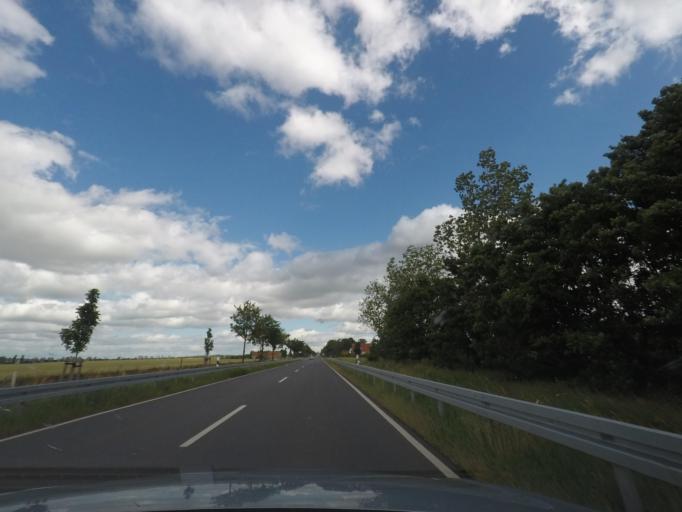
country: DE
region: Saxony-Anhalt
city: Harsleben
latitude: 51.8260
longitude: 11.1188
